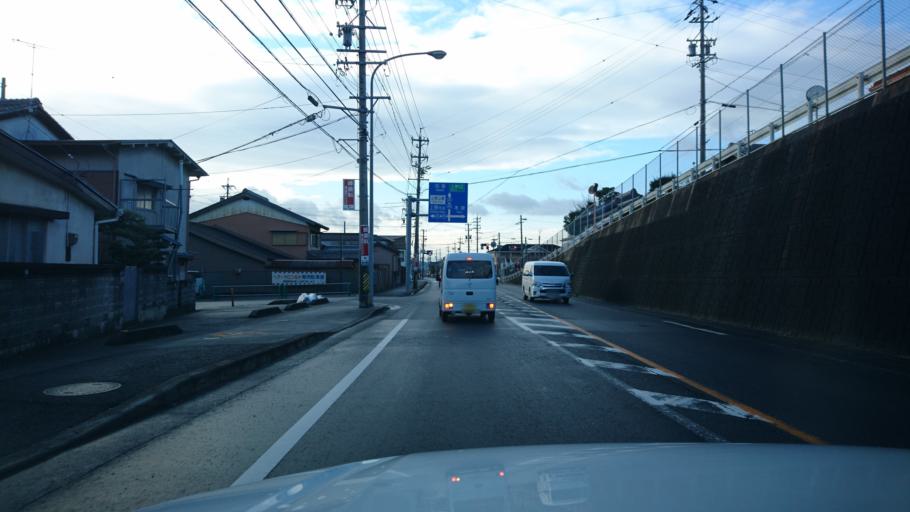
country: JP
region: Mie
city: Ueno-ebisumachi
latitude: 34.7682
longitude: 136.1233
